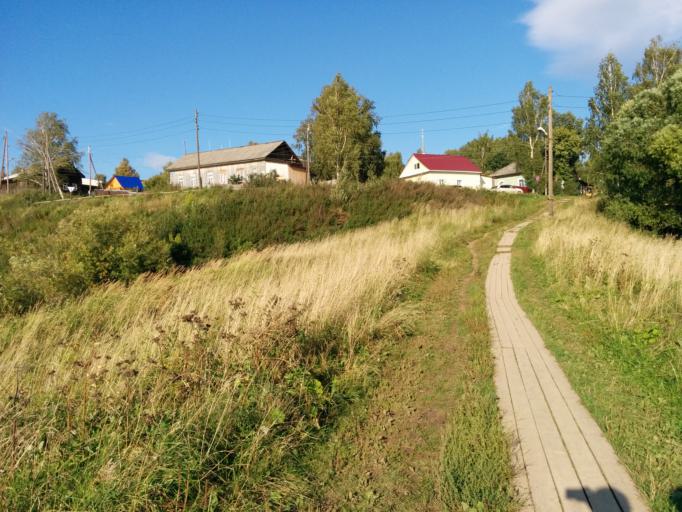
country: RU
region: Perm
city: Kudymkar
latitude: 59.0115
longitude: 54.6502
